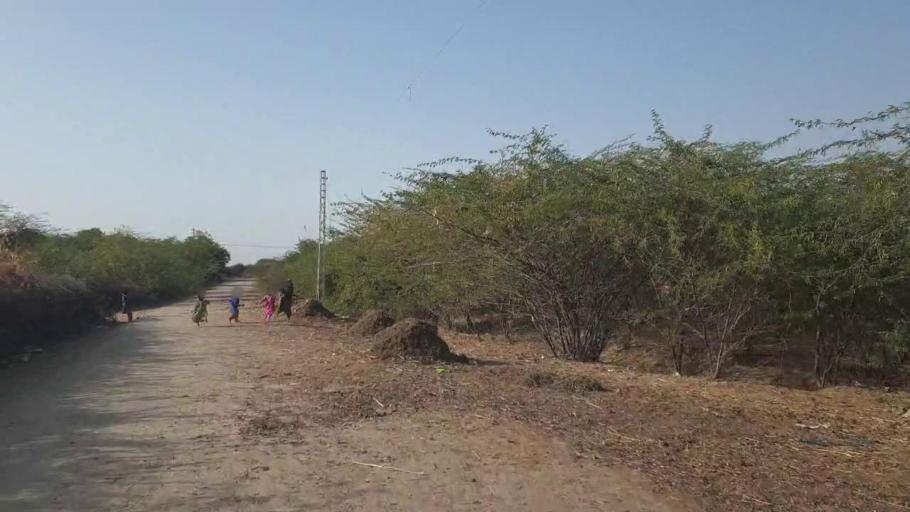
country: PK
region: Sindh
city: Dhoro Naro
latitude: 25.4723
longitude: 69.5629
